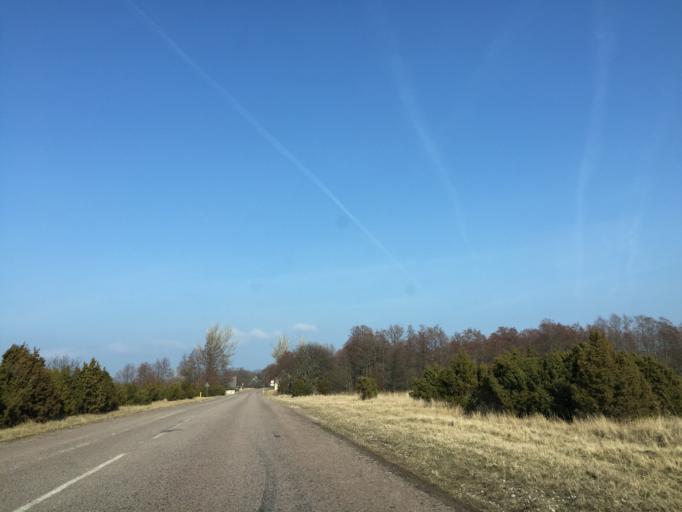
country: EE
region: Saare
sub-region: Kuressaare linn
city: Kuressaare
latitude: 58.0030
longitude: 22.0395
